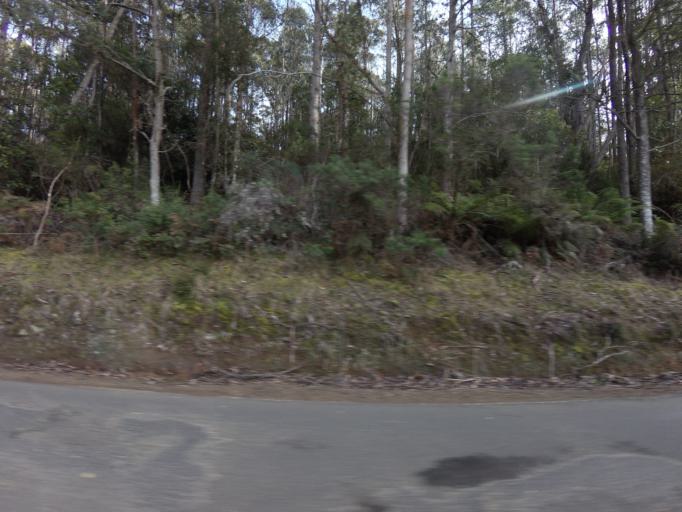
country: AU
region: Tasmania
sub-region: Kingborough
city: Margate
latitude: -43.0107
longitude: 147.1661
